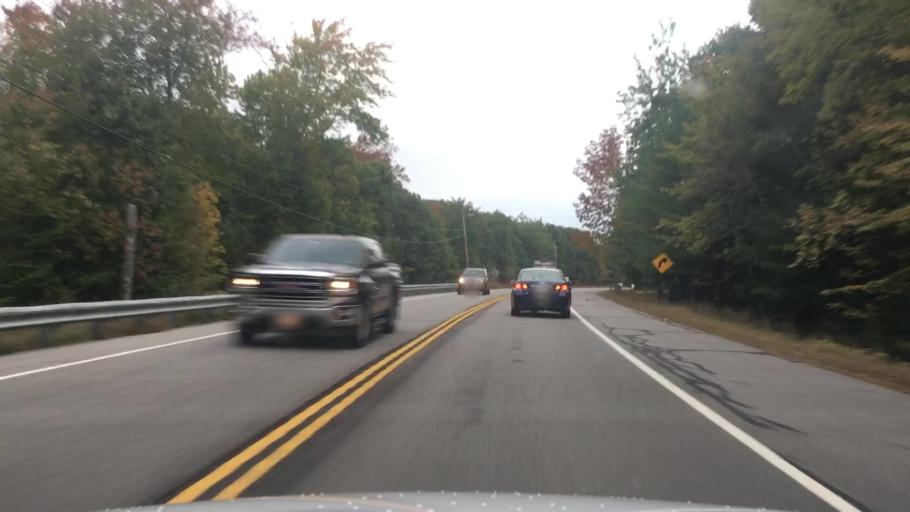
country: US
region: Maine
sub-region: York County
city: Hollis Center
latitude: 43.5974
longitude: -70.6119
